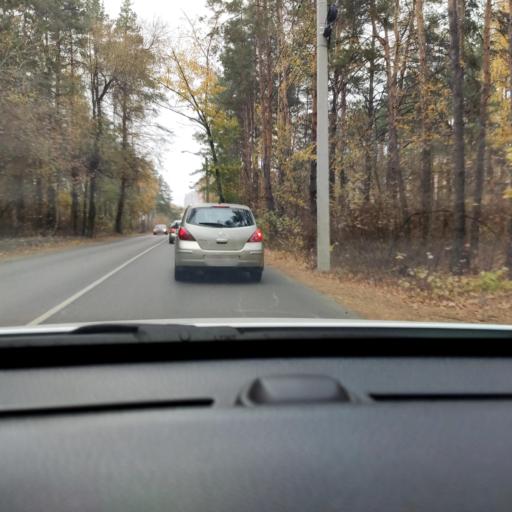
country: RU
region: Voronezj
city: Voronezh
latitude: 51.6850
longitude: 39.2780
